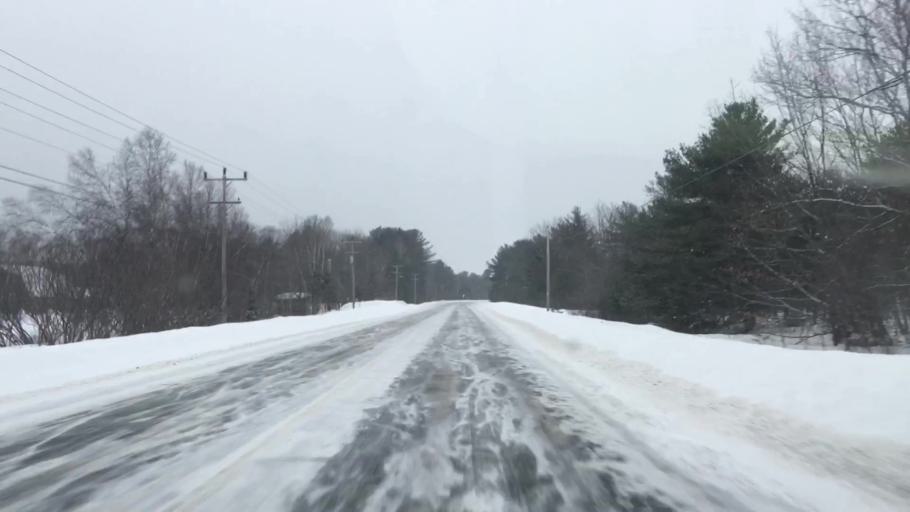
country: US
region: Maine
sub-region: Penobscot County
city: Medway
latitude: 45.5626
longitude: -68.3947
